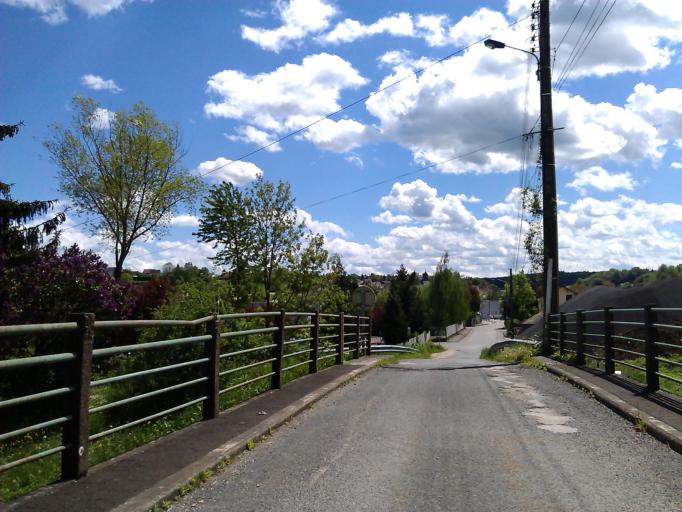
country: FR
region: Franche-Comte
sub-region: Departement du Doubs
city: Etupes
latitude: 47.5128
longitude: 6.8585
